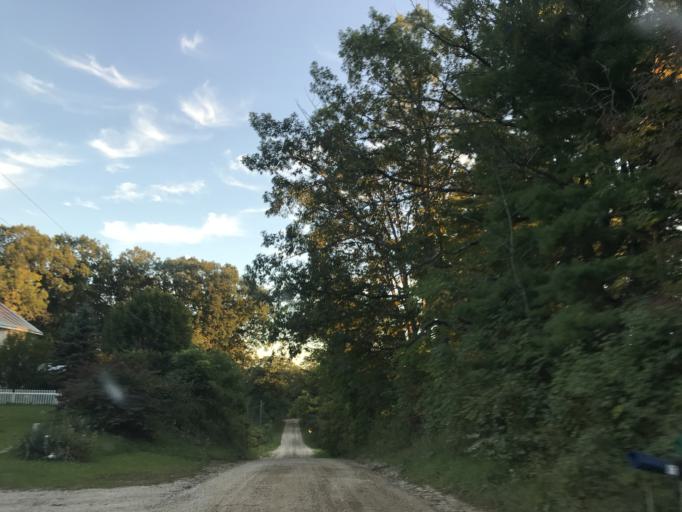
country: US
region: Michigan
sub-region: Mason County
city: Scottville
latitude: 43.9209
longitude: -86.1688
